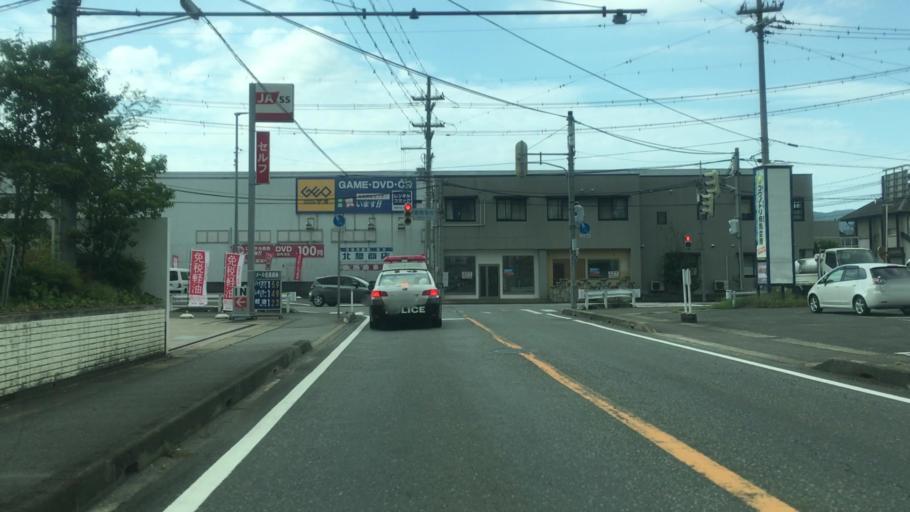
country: JP
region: Hyogo
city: Toyooka
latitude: 35.5343
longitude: 134.8198
